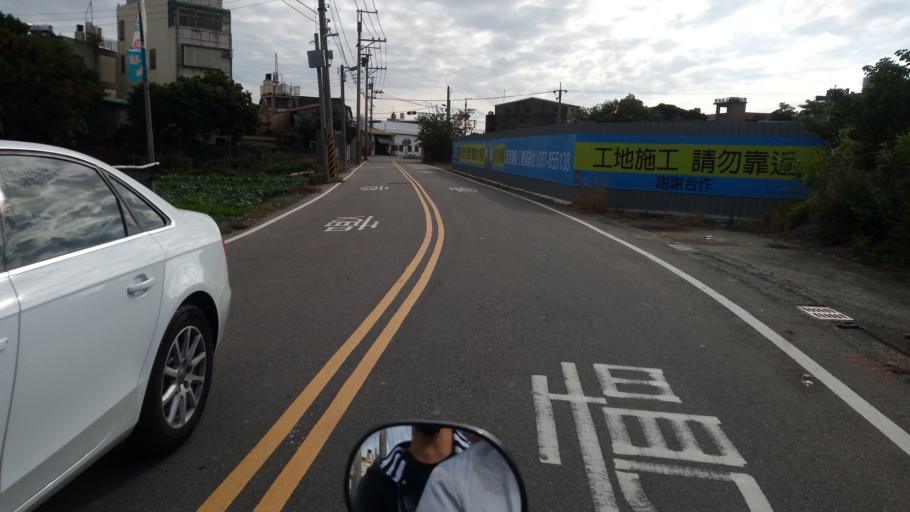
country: TW
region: Taiwan
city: Fengyuan
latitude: 24.4301
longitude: 120.6622
